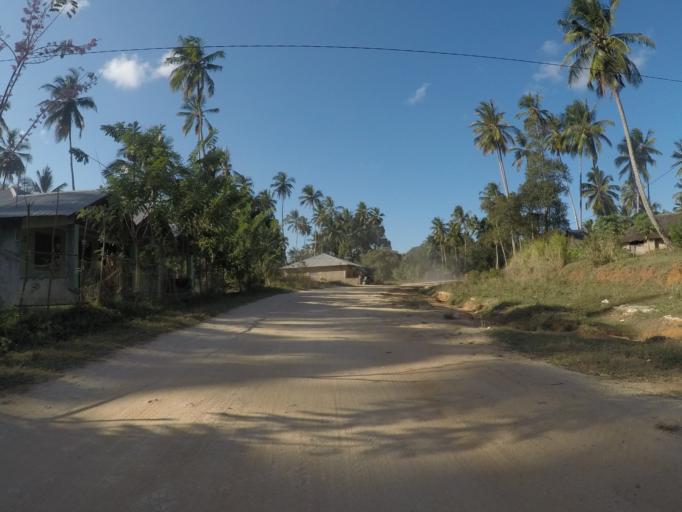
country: TZ
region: Zanzibar Central/South
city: Koani
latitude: -6.1759
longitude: 39.2835
